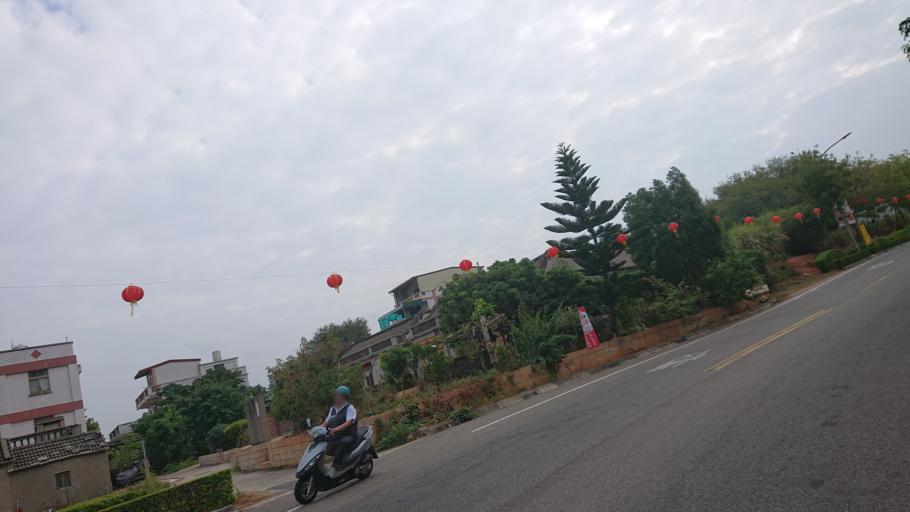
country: TW
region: Fukien
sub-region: Kinmen
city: Jincheng
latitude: 24.4119
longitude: 118.2980
